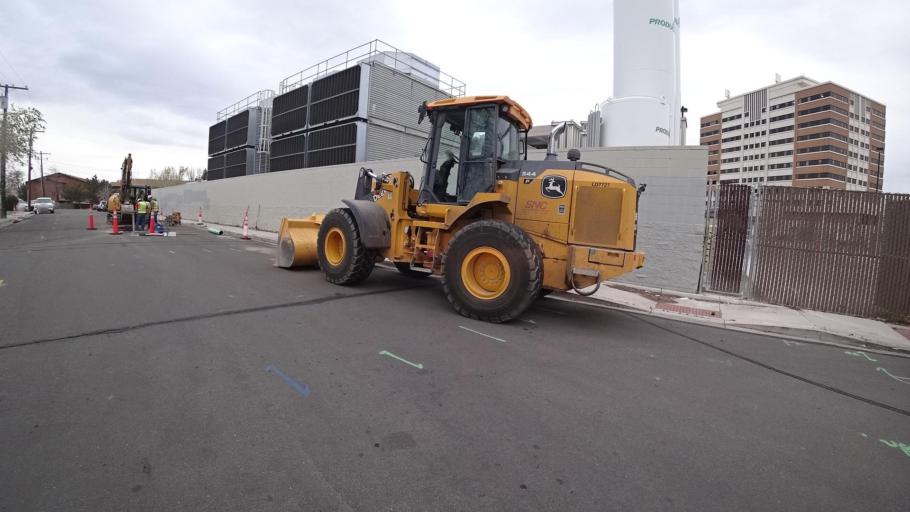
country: US
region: Nevada
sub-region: Washoe County
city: Reno
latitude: 39.5262
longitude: -119.7931
